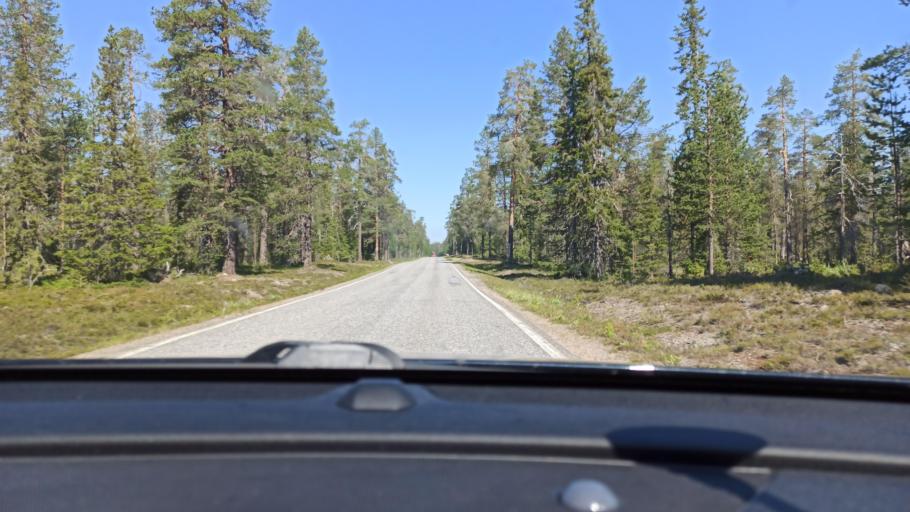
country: FI
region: Lapland
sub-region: Tunturi-Lappi
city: Kolari
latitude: 67.6614
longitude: 24.1651
